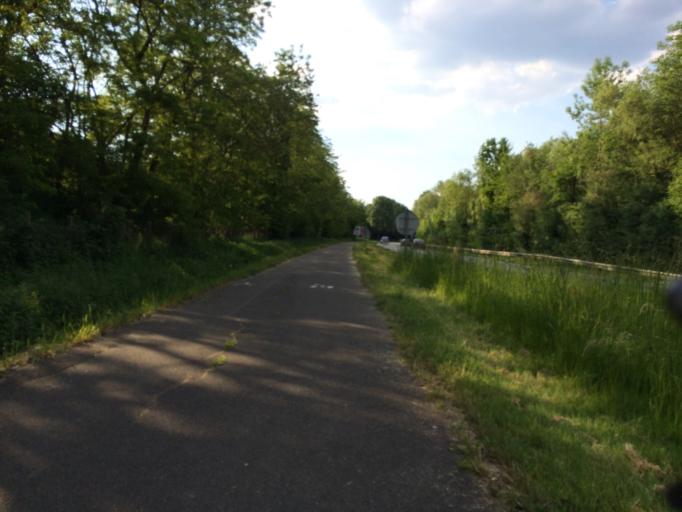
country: FR
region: Ile-de-France
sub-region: Departement de l'Essonne
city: Lisses
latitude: 48.6049
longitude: 2.4278
